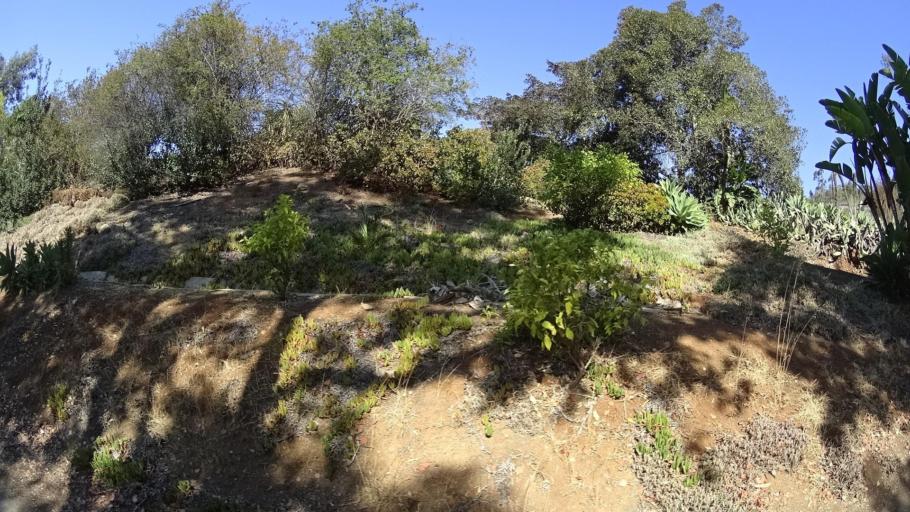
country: US
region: California
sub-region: San Diego County
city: Rancho Santa Fe
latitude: 33.0348
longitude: -117.1674
